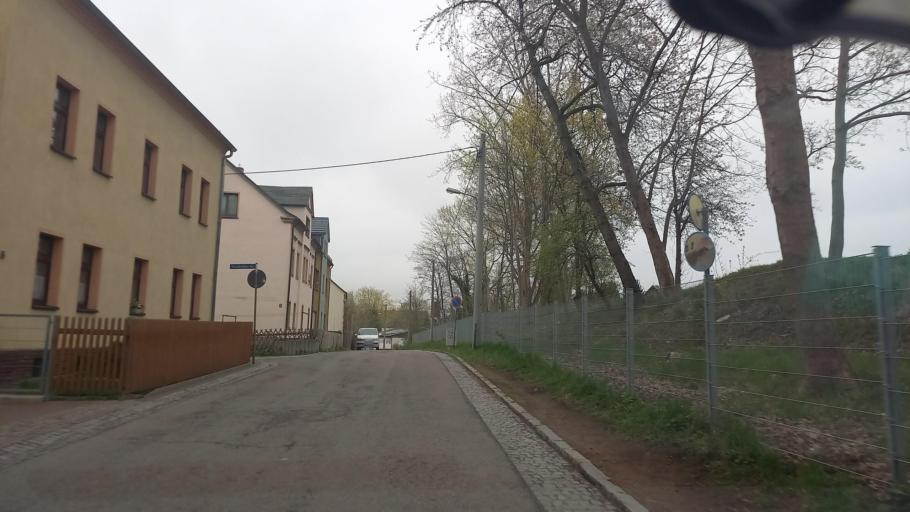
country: DE
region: Saxony
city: Zwickau
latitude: 50.6924
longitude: 12.4760
